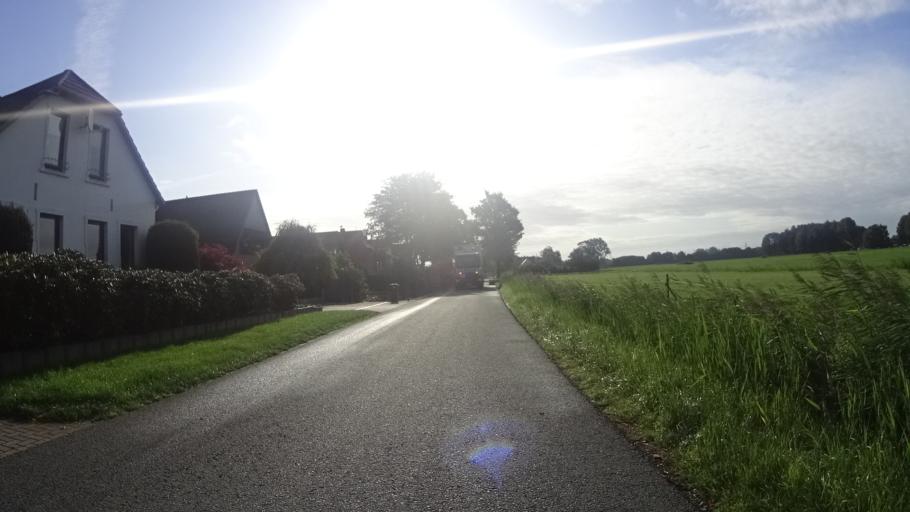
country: DE
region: Lower Saxony
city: Nordenham
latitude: 53.4946
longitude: 8.4477
